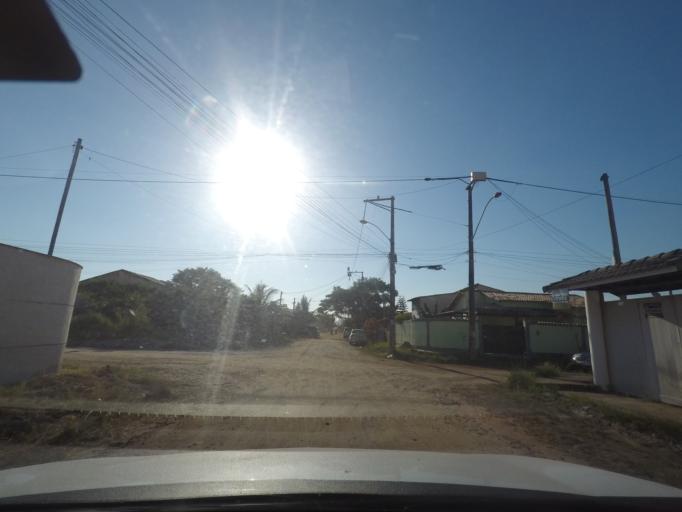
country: BR
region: Rio de Janeiro
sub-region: Marica
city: Marica
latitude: -22.9620
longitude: -42.9494
